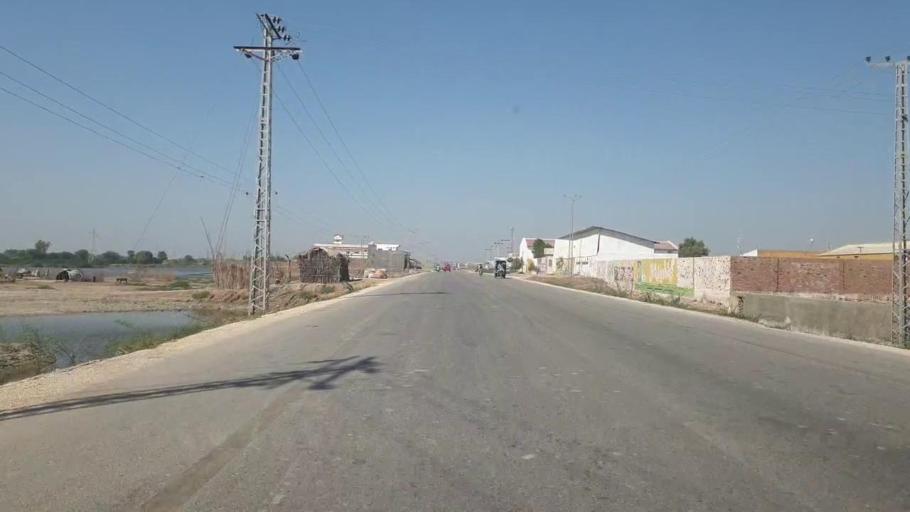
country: PK
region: Sindh
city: Talhar
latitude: 24.8764
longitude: 68.8145
